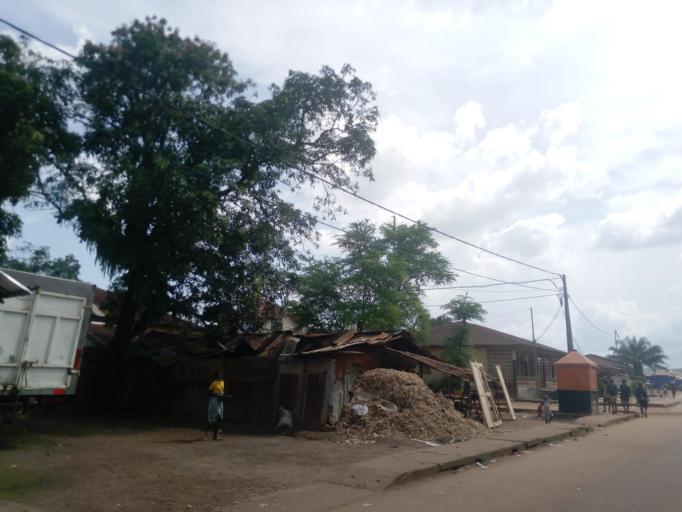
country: SL
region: Northern Province
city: Makeni
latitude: 8.8917
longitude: -12.0391
